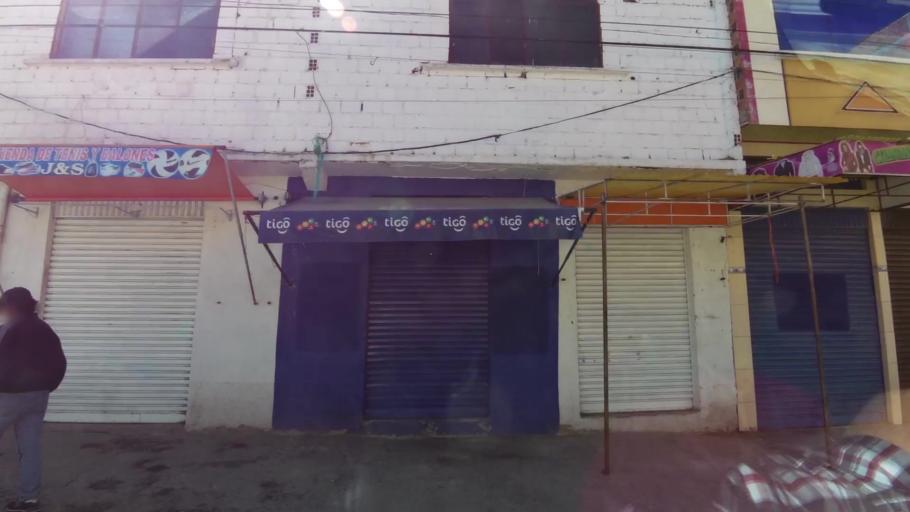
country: BO
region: La Paz
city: La Paz
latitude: -16.5133
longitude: -68.1622
